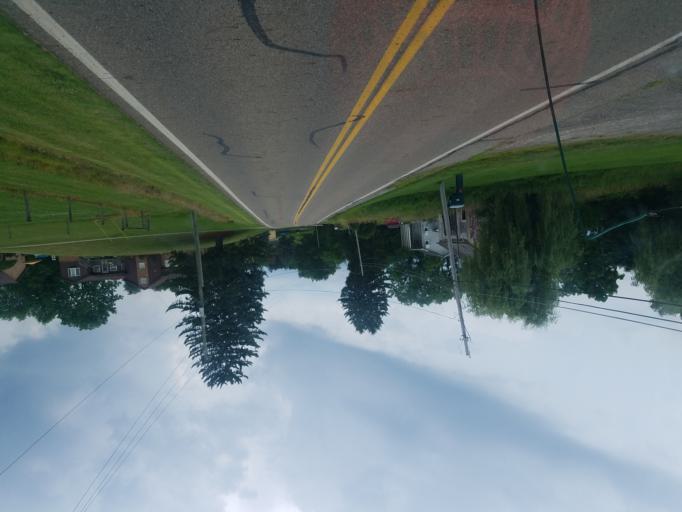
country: US
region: Ohio
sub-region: Stark County
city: Hartville
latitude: 41.0259
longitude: -81.3107
